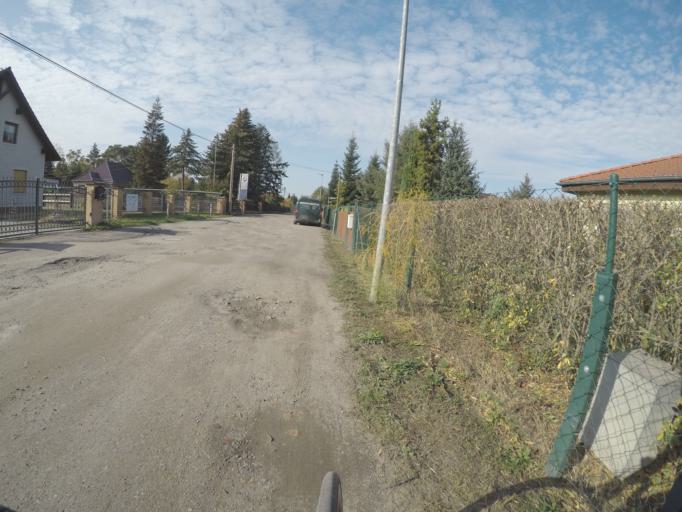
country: DE
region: Brandenburg
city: Oranienburg
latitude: 52.7437
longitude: 13.2175
